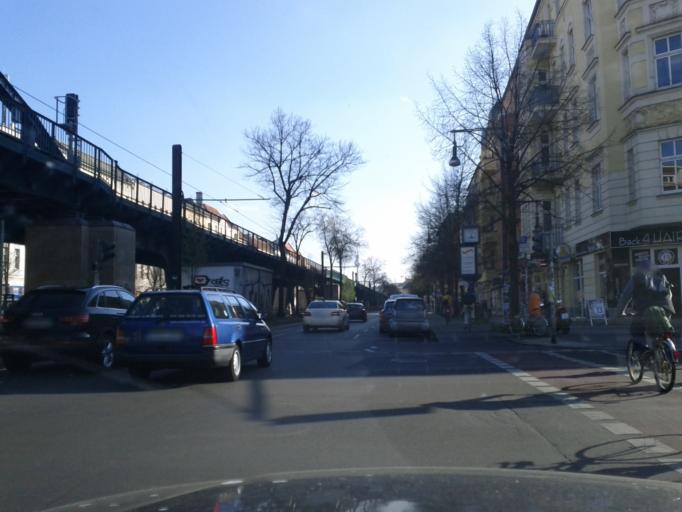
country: DE
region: Berlin
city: Prenzlauer Berg Bezirk
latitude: 52.5477
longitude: 13.4133
